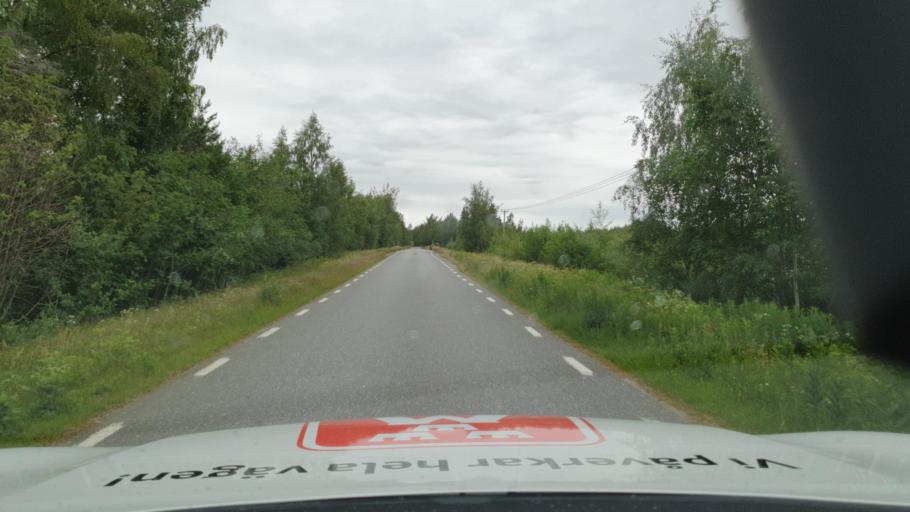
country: SE
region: Vaesterbotten
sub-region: Nordmalings Kommun
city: Nordmaling
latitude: 63.4666
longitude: 19.4645
